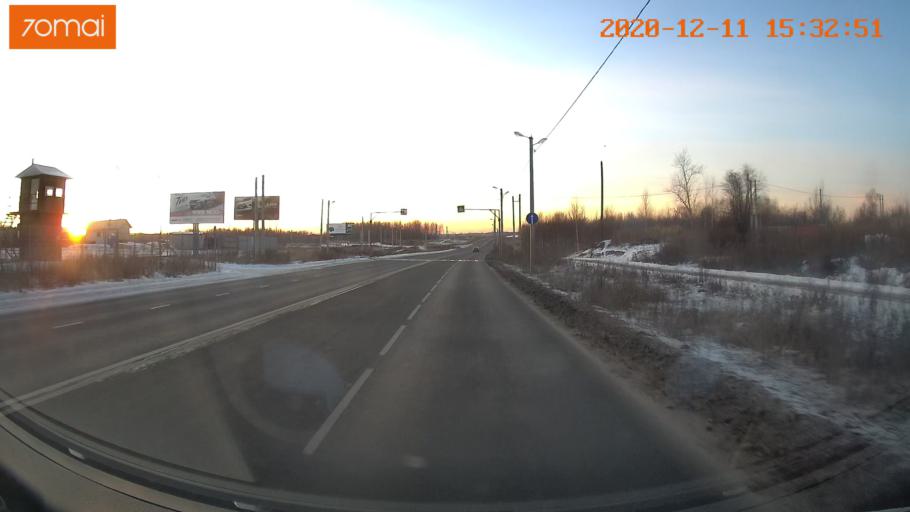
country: RU
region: Ivanovo
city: Bogorodskoye
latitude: 57.0527
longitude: 40.9596
